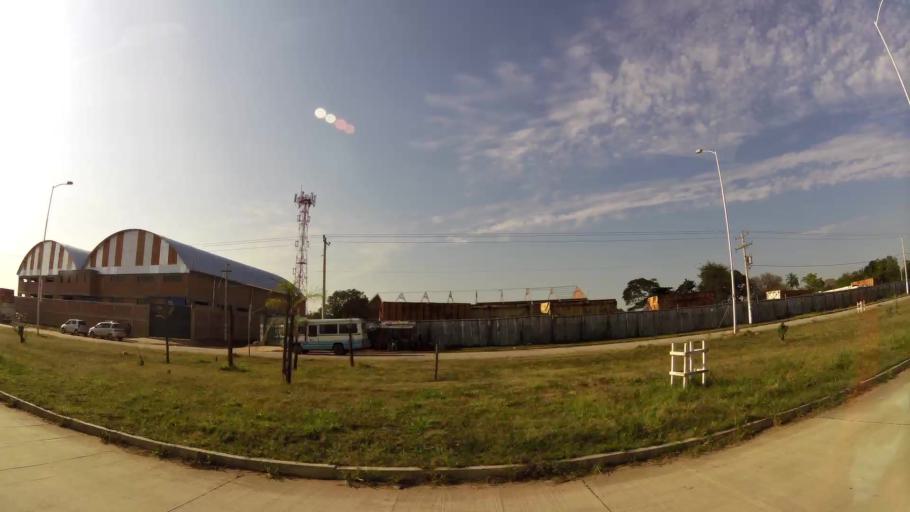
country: BO
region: Santa Cruz
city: Santa Cruz de la Sierra
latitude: -17.7002
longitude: -63.1275
